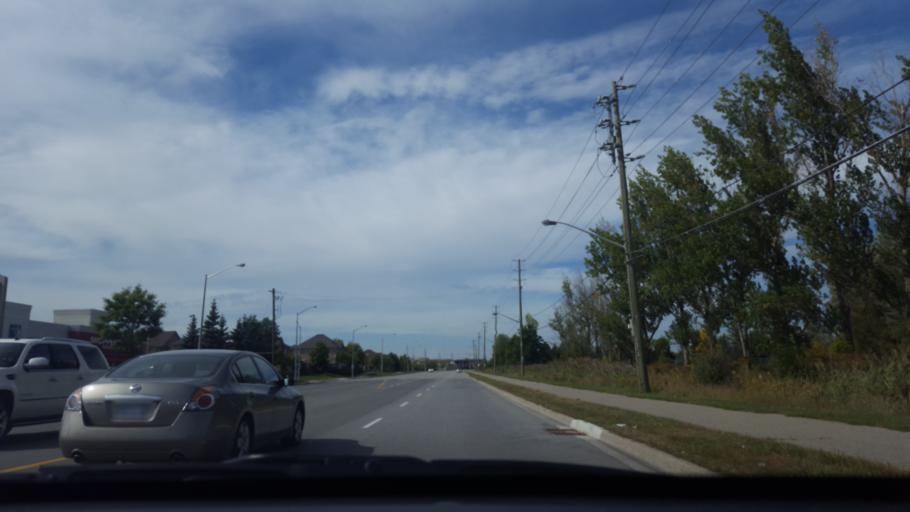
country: CA
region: Ontario
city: Vaughan
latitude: 43.8180
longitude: -79.6016
